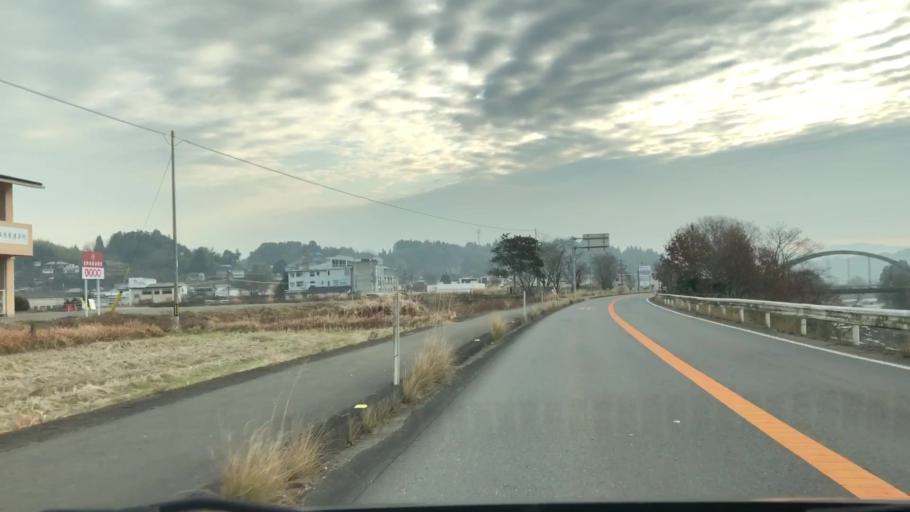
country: JP
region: Oita
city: Takedamachi
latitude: 32.9696
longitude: 131.4708
